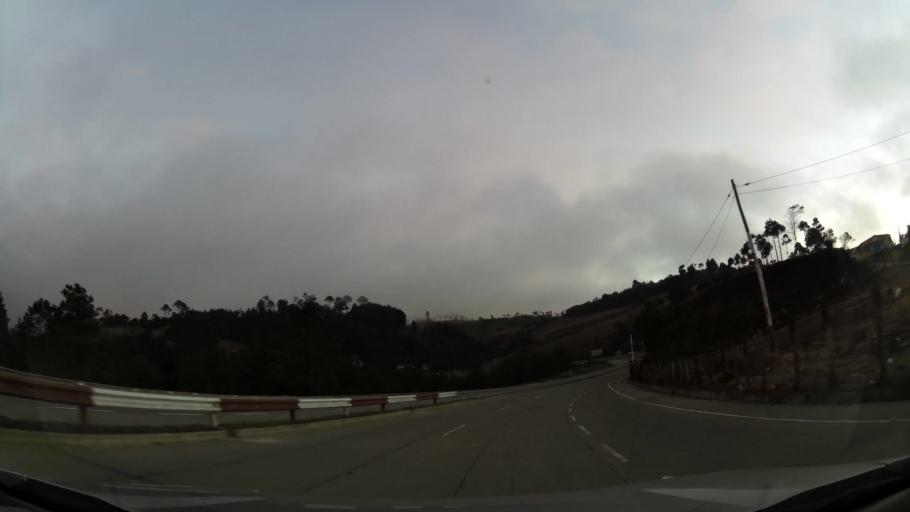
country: GT
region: Solola
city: Concepcion
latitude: 14.8296
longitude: -91.0940
